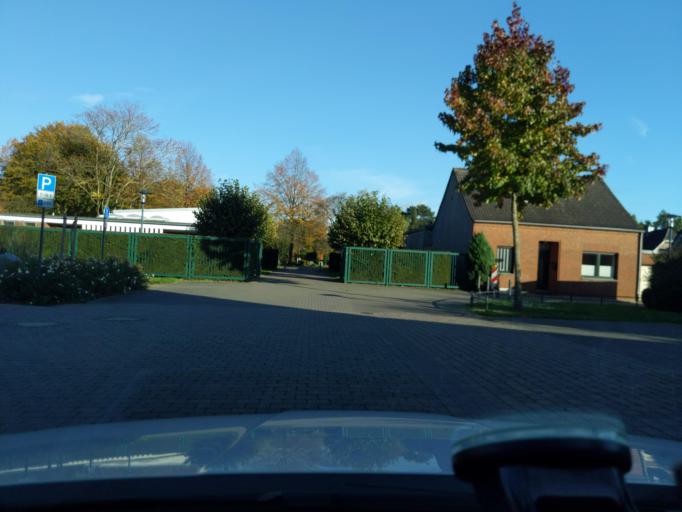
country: DE
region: North Rhine-Westphalia
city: Kempen
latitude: 51.3856
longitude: 6.4531
